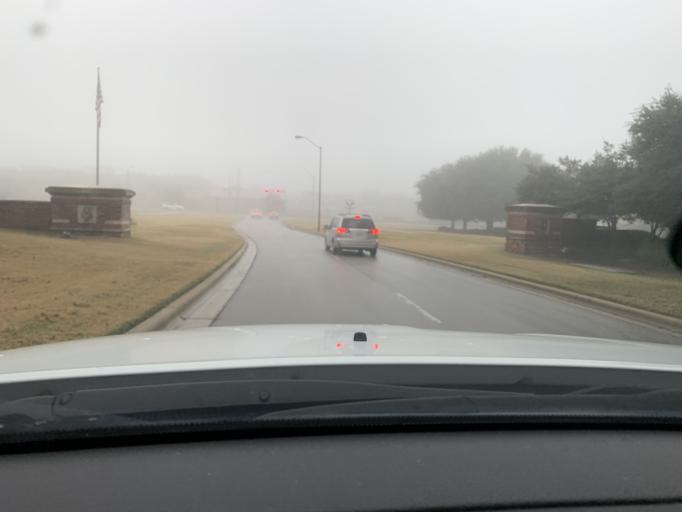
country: US
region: Texas
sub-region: Williamson County
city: Round Rock
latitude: 30.5668
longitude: -97.6701
